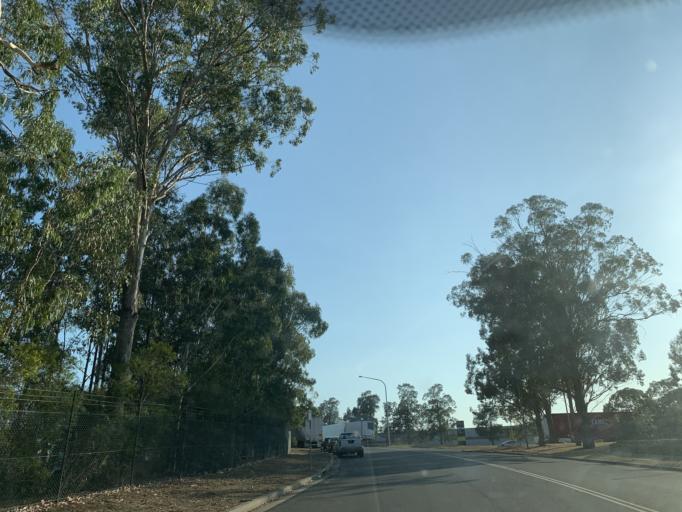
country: AU
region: New South Wales
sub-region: Blacktown
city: Doonside
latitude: -33.7982
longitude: 150.8871
